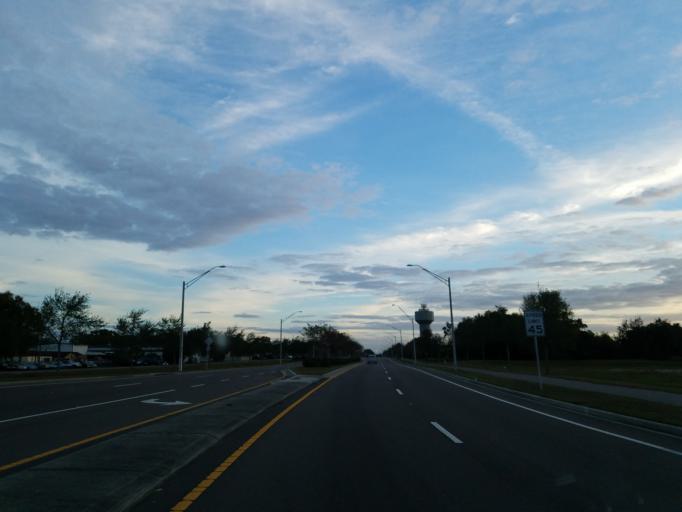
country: US
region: Florida
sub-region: Hillsborough County
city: Egypt Lake-Leto
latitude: 27.9912
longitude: -82.5200
